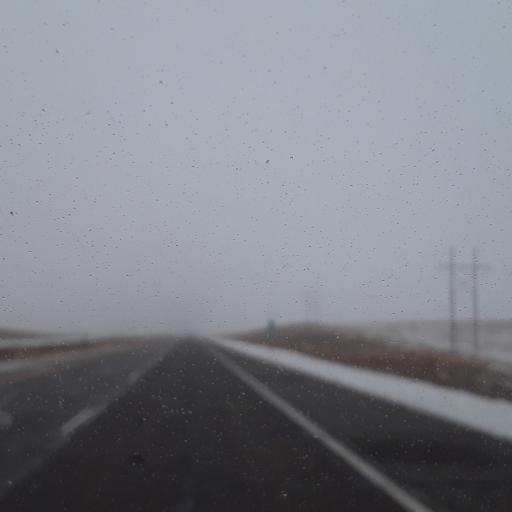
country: US
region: Nebraska
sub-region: Cheyenne County
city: Sidney
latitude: 40.7985
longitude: -102.8720
